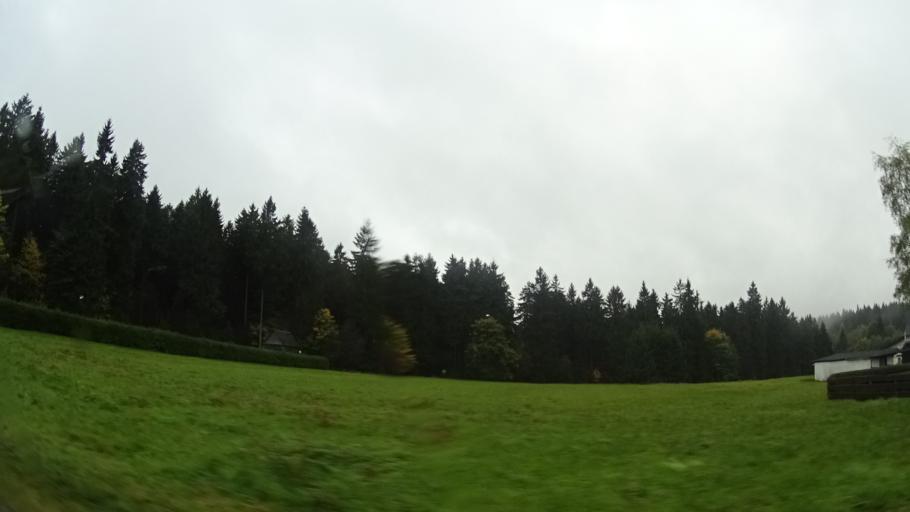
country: DE
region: Bavaria
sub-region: Upper Franconia
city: Tschirn
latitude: 50.4357
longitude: 11.4692
